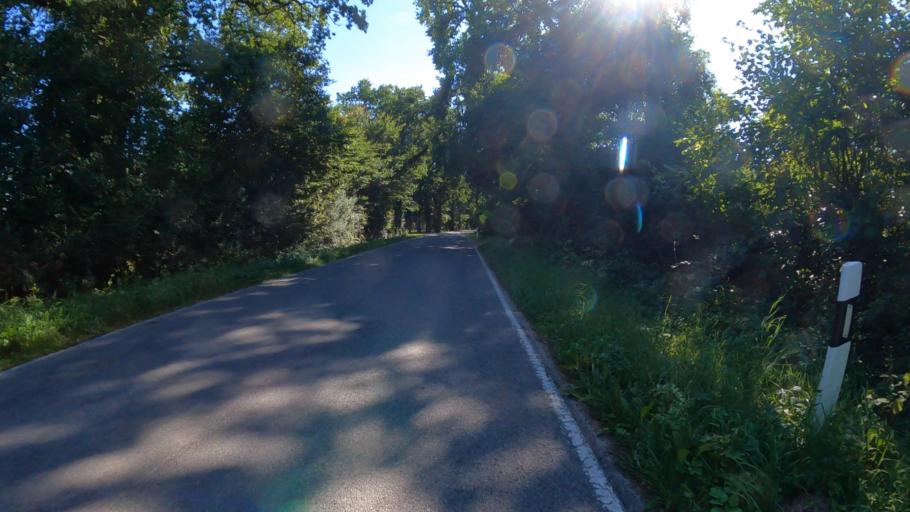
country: DE
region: Schleswig-Holstein
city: Westerau
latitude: 53.7713
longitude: 10.5168
